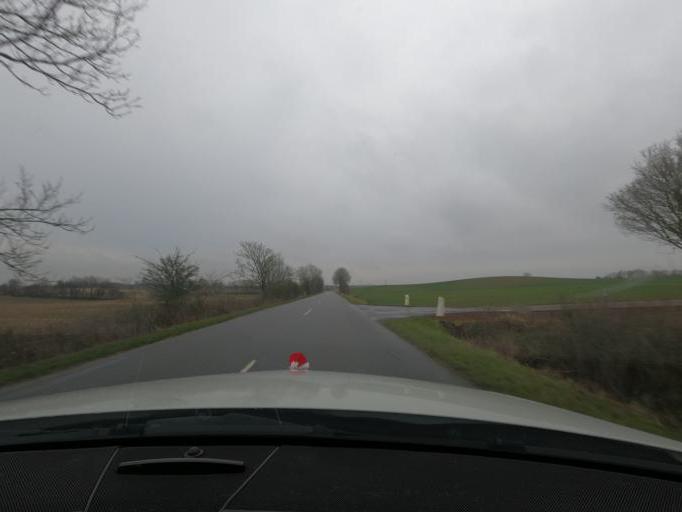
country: DK
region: South Denmark
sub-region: Haderslev Kommune
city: Haderslev
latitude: 55.1960
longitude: 9.4656
